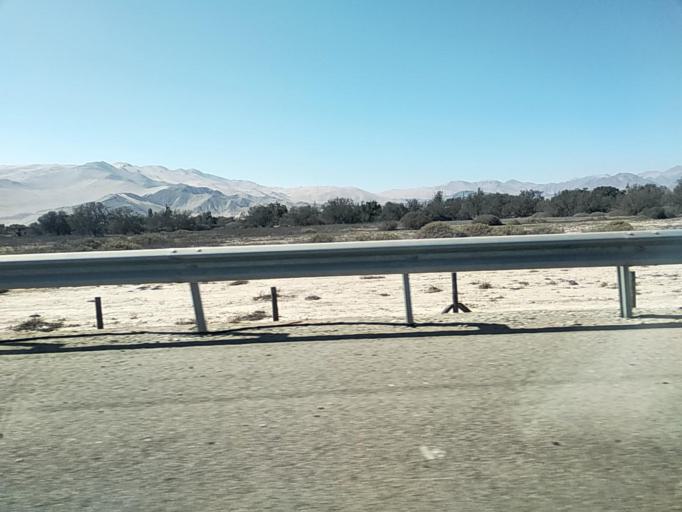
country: CL
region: Atacama
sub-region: Provincia de Copiapo
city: Copiapo
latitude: -27.3048
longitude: -70.4301
